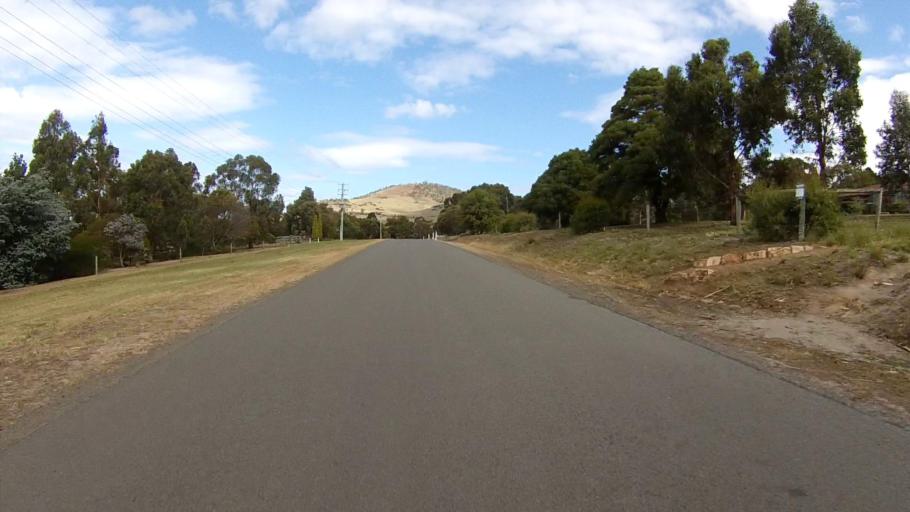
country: AU
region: Tasmania
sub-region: Clarence
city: Acton Park
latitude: -42.8595
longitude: 147.4839
